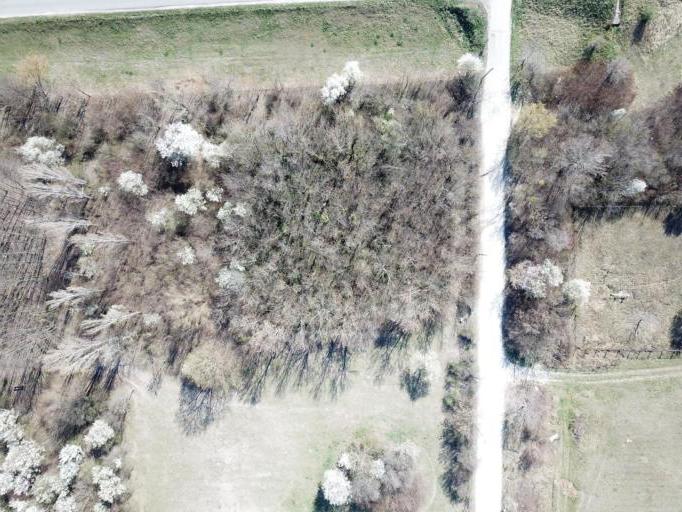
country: HU
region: Pest
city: Budakalasz
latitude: 47.6086
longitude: 19.0700
